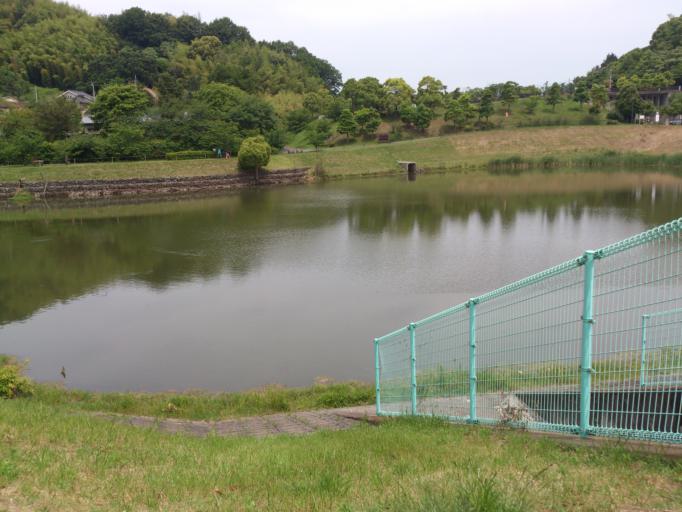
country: JP
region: Ehime
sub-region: Shikoku-chuo Shi
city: Matsuyama
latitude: 33.8400
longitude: 132.7365
